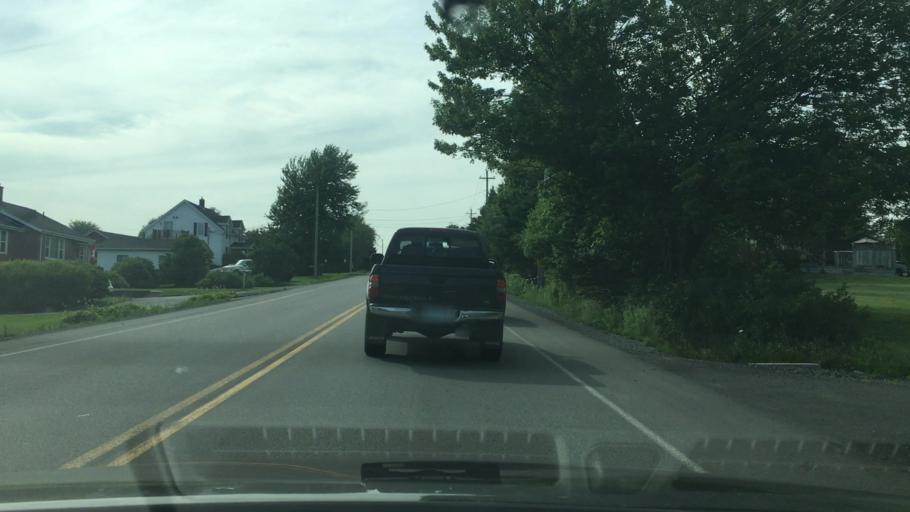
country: CA
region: Nova Scotia
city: Dartmouth
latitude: 44.7300
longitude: -63.7520
